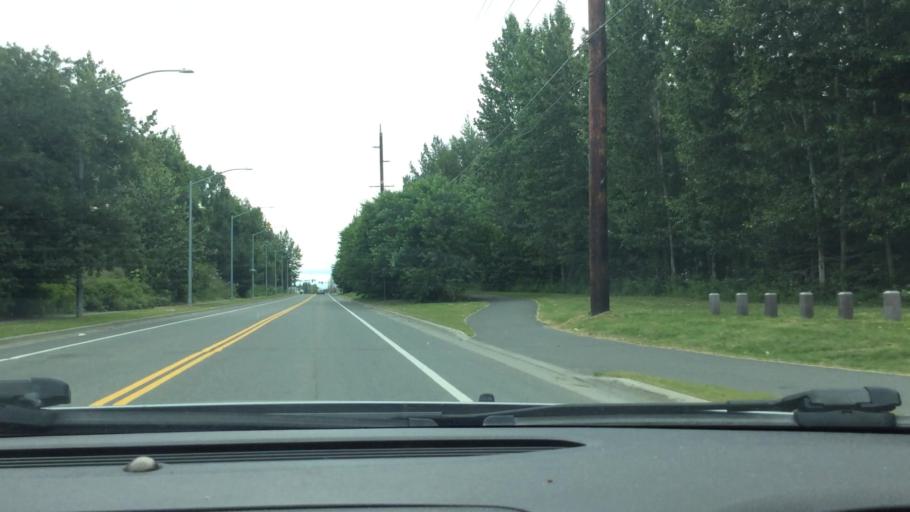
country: US
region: Alaska
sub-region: Anchorage Municipality
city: Anchorage
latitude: 61.2058
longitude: -149.7934
